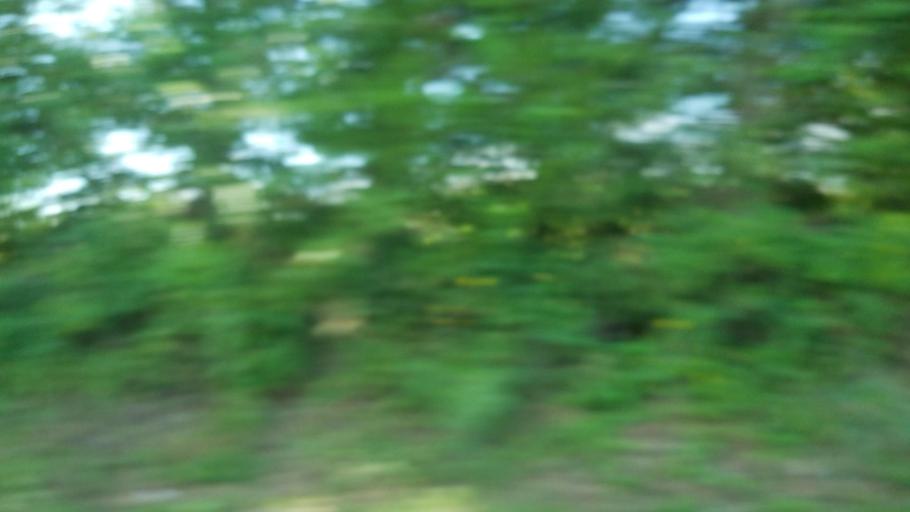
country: US
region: Illinois
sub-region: Williamson County
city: Johnston City
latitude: 37.7874
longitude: -88.8175
